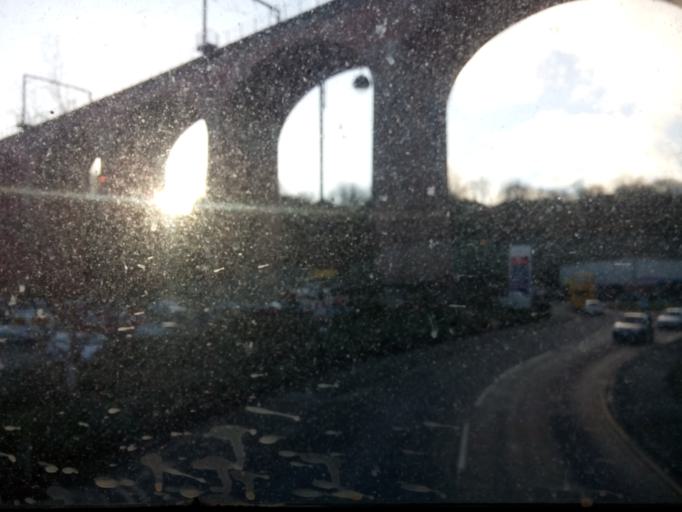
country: GB
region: England
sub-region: County Durham
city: Chester-le-Street
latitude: 54.8589
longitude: -1.5788
